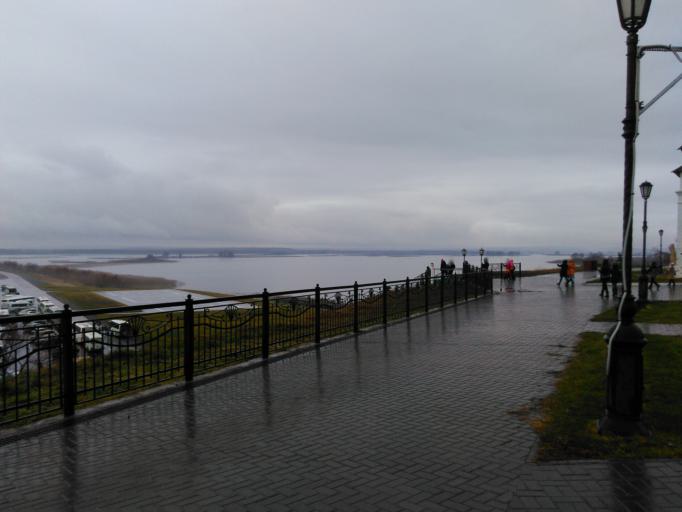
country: RU
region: Tatarstan
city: Sviyazhsk
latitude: 55.7693
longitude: 48.6530
